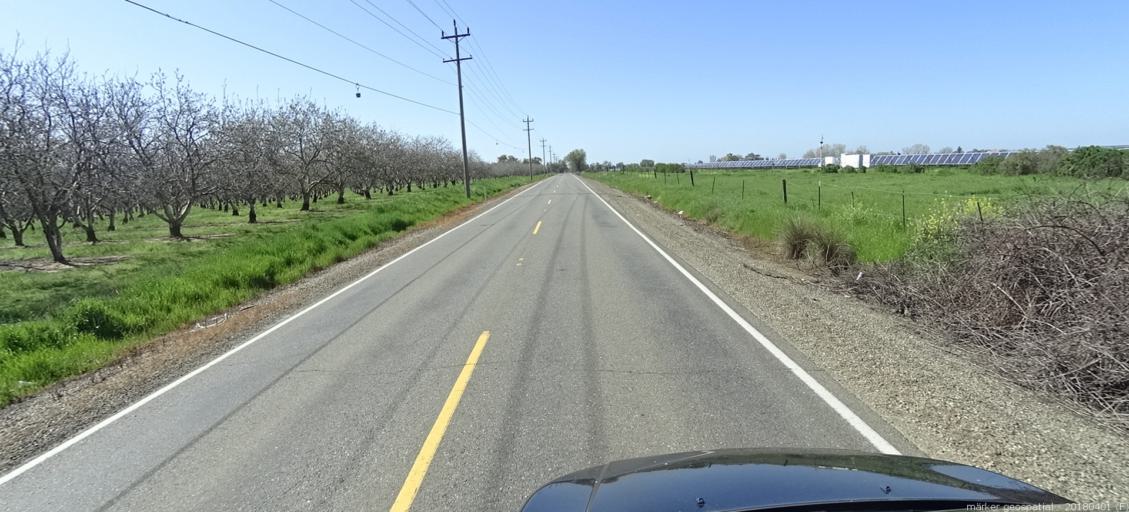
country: US
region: California
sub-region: Sacramento County
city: Rancho Murieta
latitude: 38.4654
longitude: -121.1766
